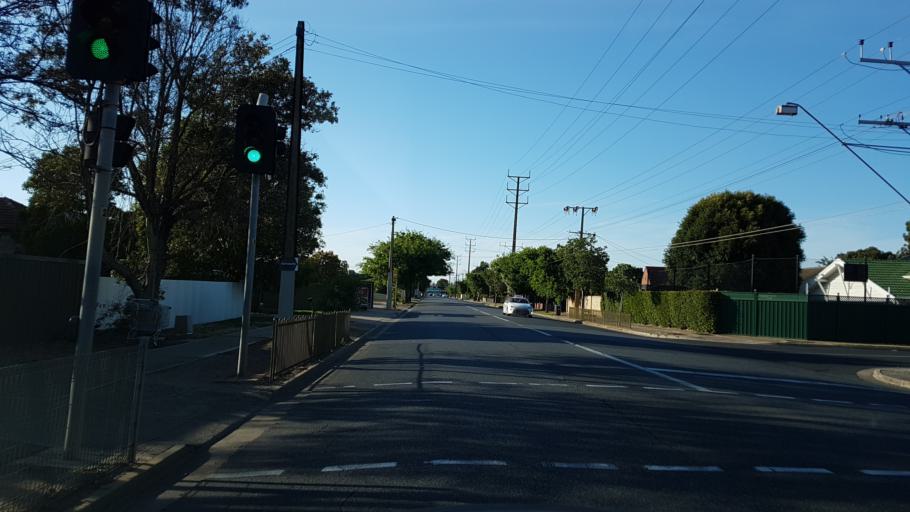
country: AU
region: South Australia
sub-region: City of West Torrens
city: Thebarton
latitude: -34.9227
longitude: 138.5488
